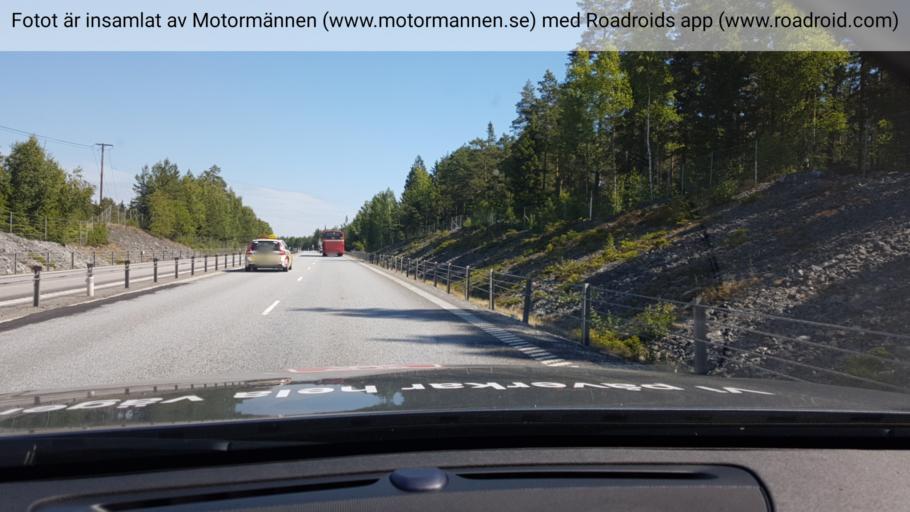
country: SE
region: Stockholm
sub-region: Osterakers Kommun
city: Akersberga
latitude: 59.5949
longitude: 18.2694
